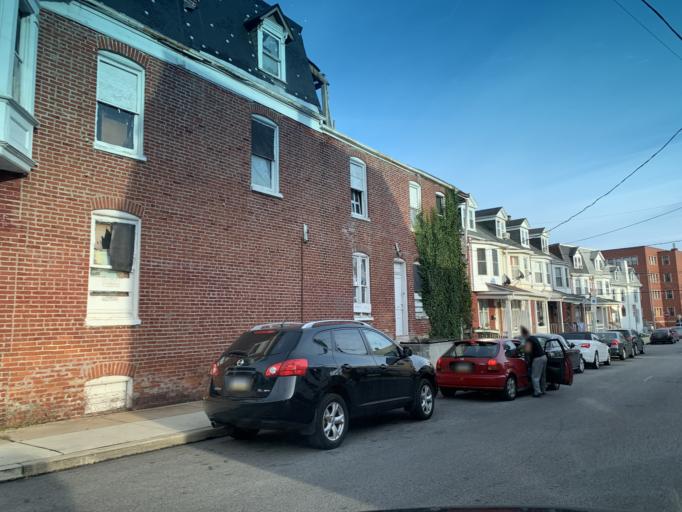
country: US
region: Pennsylvania
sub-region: York County
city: West York
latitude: 39.9542
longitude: -76.7414
